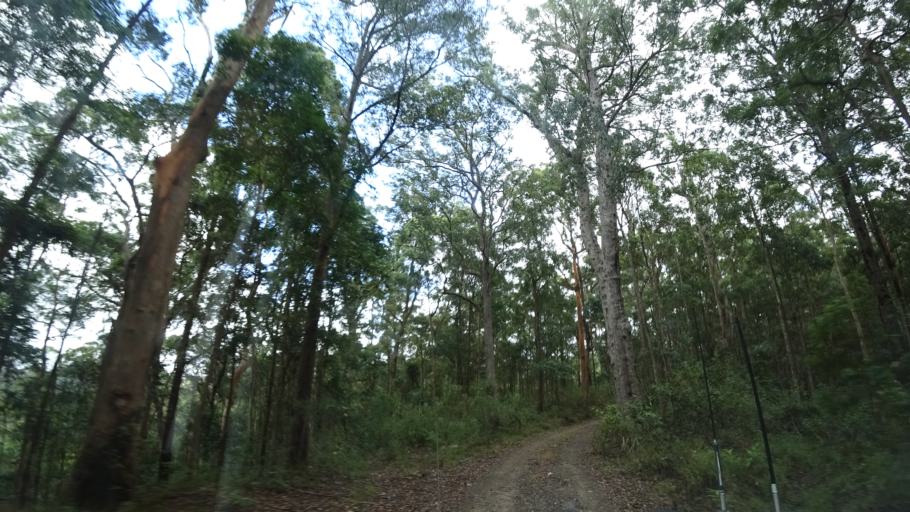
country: AU
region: Queensland
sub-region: Moreton Bay
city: Highvale
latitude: -27.4173
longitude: 152.8113
